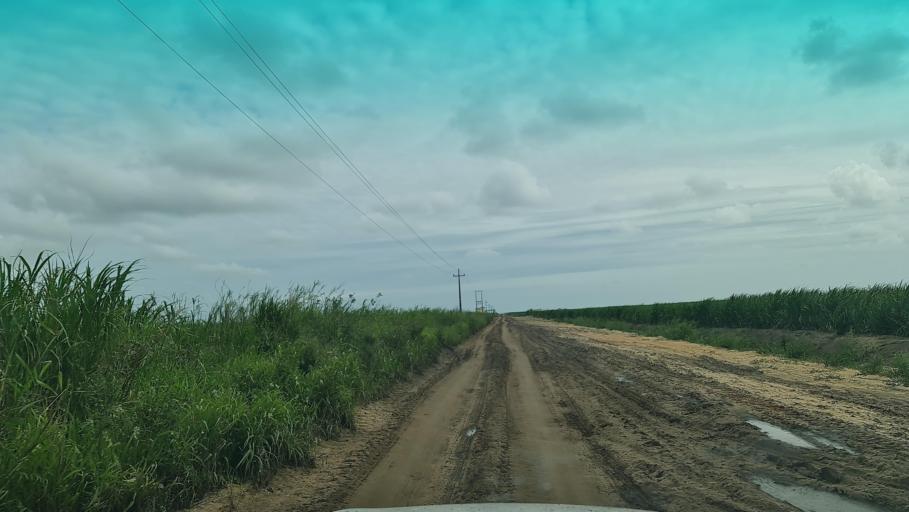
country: MZ
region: Maputo
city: Manhica
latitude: -25.4515
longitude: 32.8391
